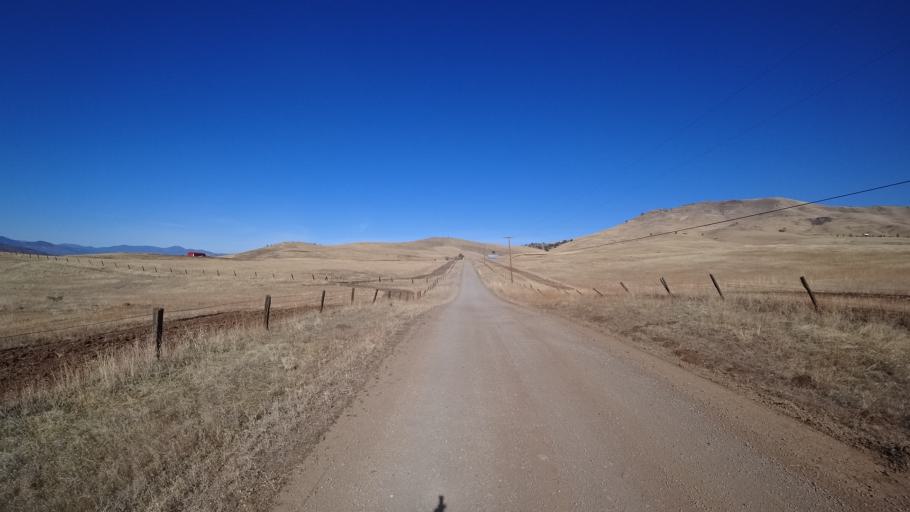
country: US
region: California
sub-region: Siskiyou County
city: Montague
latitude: 41.8382
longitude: -122.4206
